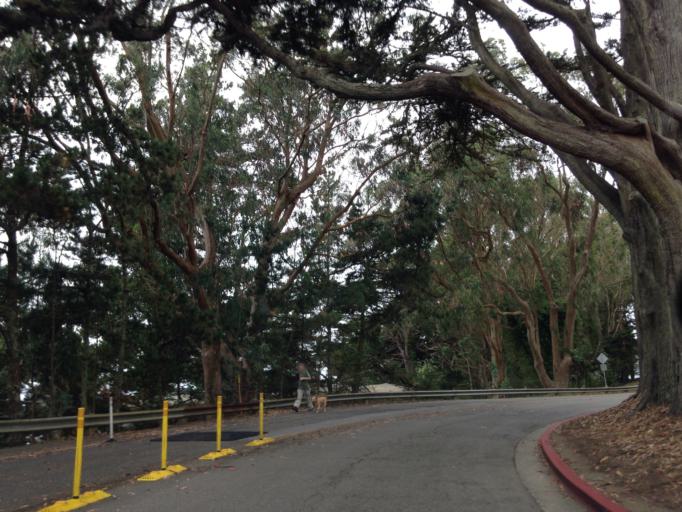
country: US
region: California
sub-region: San Francisco County
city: San Francisco
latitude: 37.7937
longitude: -122.4753
